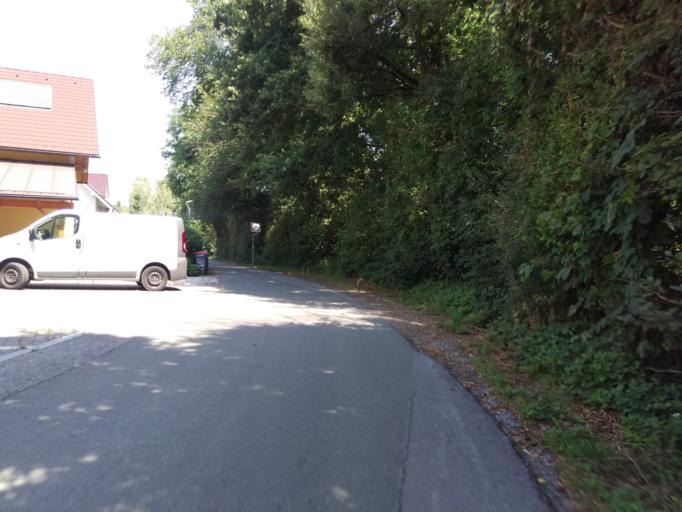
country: AT
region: Styria
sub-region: Politischer Bezirk Graz-Umgebung
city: Gossendorf
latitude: 46.9865
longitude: 15.4700
